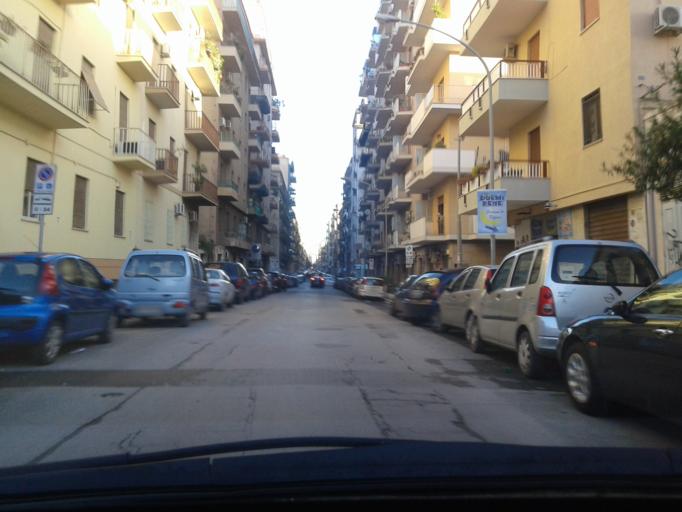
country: IT
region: Sicily
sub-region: Palermo
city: Palermo
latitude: 38.1174
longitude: 13.3464
